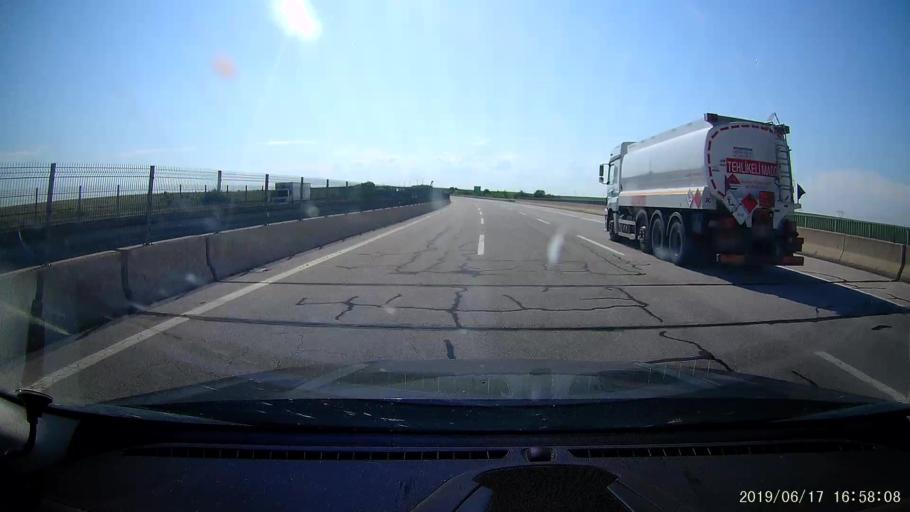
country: TR
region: Edirne
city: Haskoy
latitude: 41.6100
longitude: 26.8967
